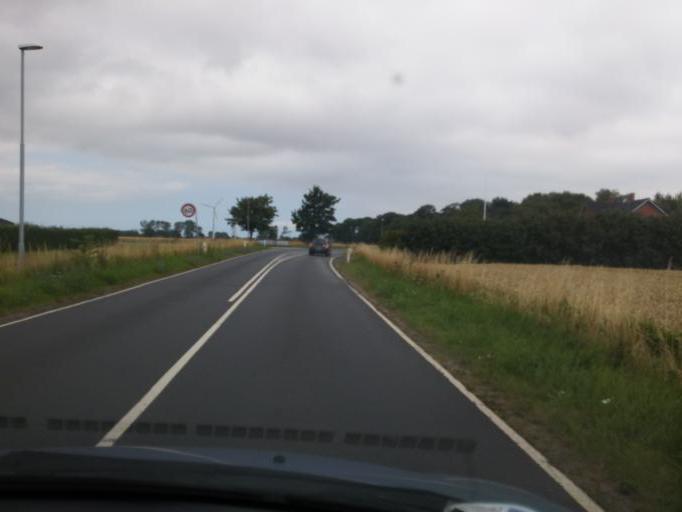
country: DK
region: South Denmark
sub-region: Kerteminde Kommune
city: Langeskov
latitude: 55.3881
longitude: 10.5284
